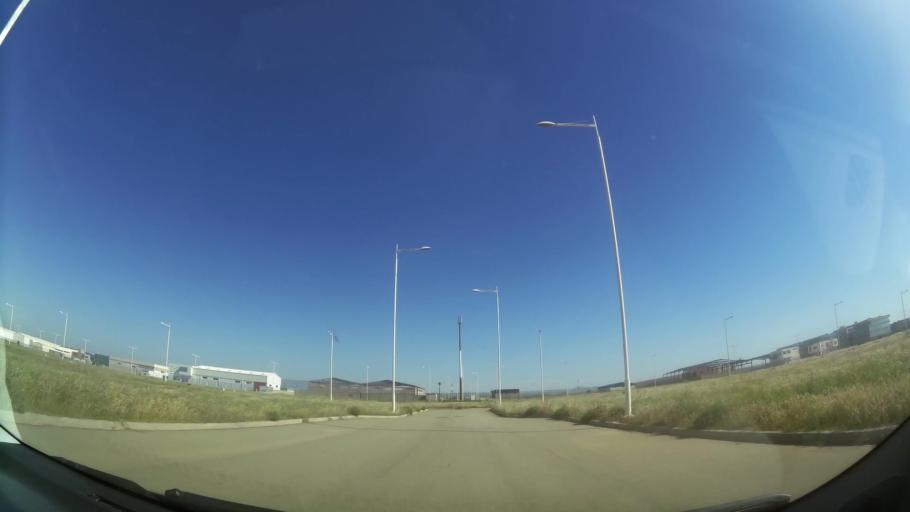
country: MA
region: Oriental
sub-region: Oujda-Angad
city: Oujda
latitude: 34.7726
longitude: -1.9352
